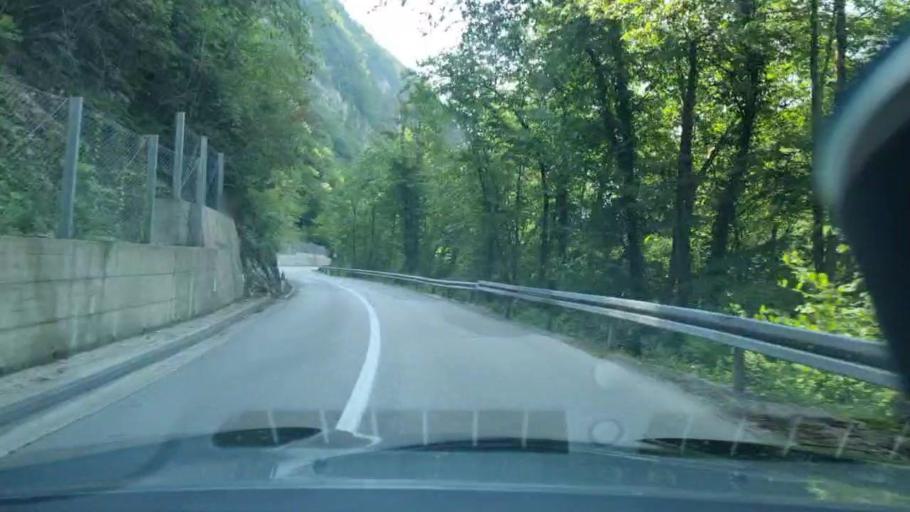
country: BA
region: Federation of Bosnia and Herzegovina
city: Stijena
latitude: 44.8808
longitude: 16.0697
